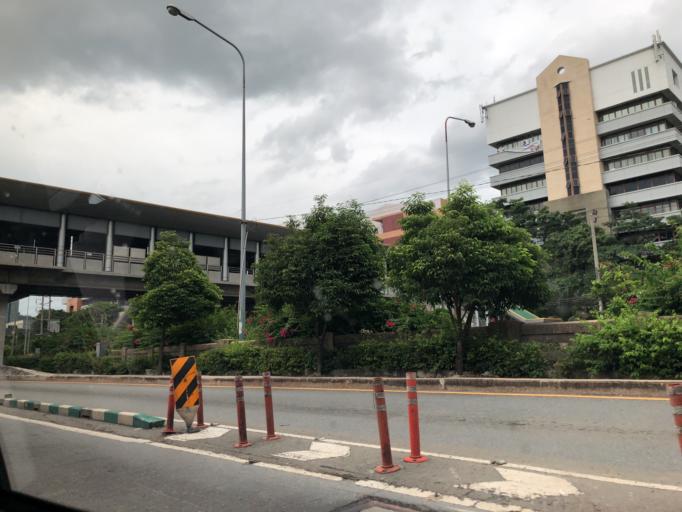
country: TH
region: Bangkok
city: Sathon
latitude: 13.7119
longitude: 100.5351
